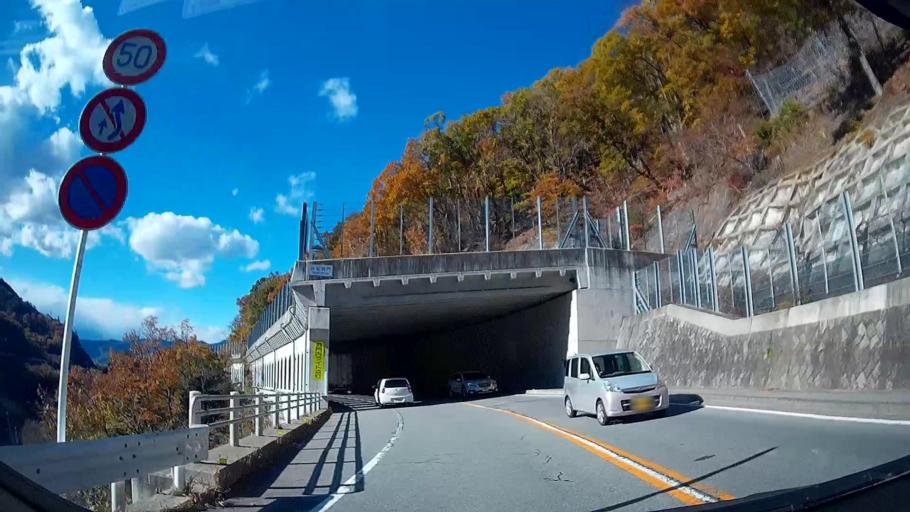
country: JP
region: Yamanashi
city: Enzan
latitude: 35.6511
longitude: 138.7568
